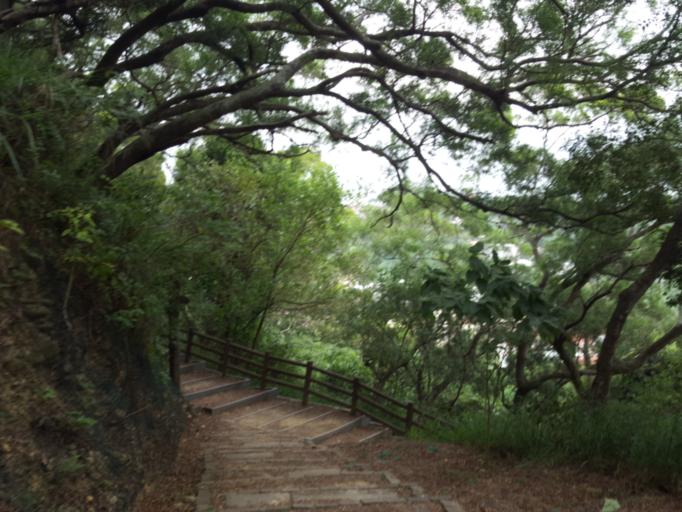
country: TW
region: Taiwan
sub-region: Hsinchu
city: Hsinchu
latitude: 24.7719
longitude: 120.9320
